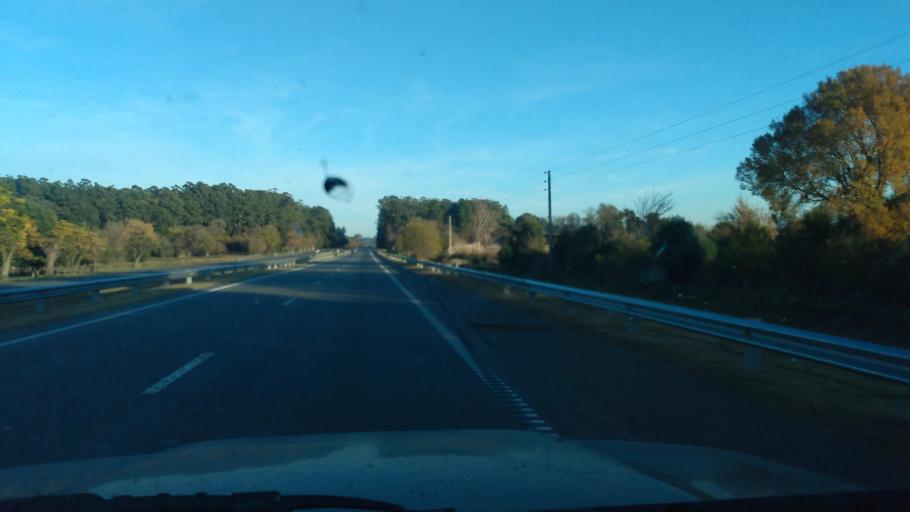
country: AR
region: Buenos Aires
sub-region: Partido de Lujan
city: Lujan
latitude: -34.5445
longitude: -59.2248
